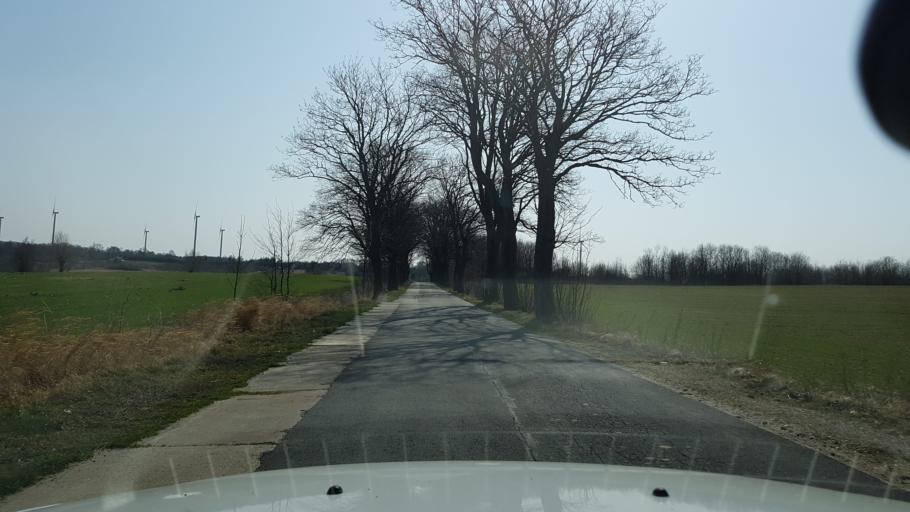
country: PL
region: West Pomeranian Voivodeship
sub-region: Powiat slawienski
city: Darlowo
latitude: 54.4868
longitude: 16.5073
